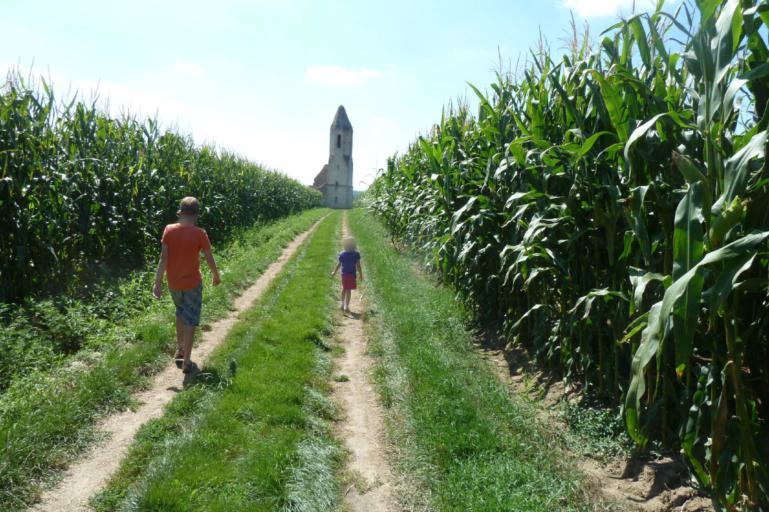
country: HU
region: Somogy
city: Somogyvar
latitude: 46.5571
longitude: 17.6797
